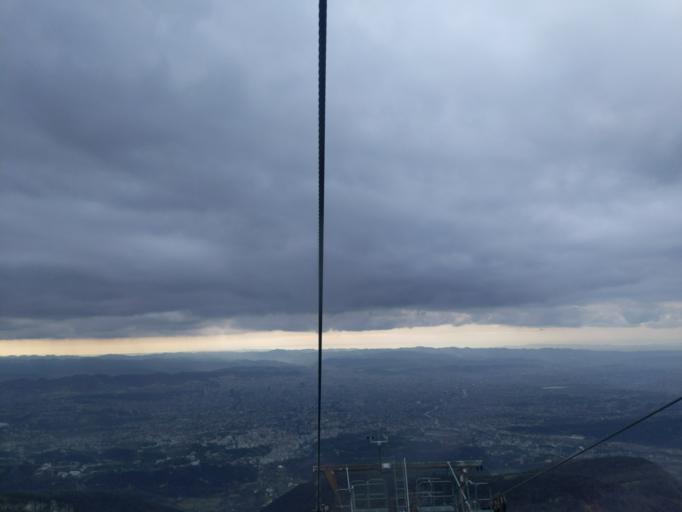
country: AL
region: Tirane
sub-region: Rrethi i Tiranes
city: Dajt
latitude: 41.3672
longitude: 19.9027
